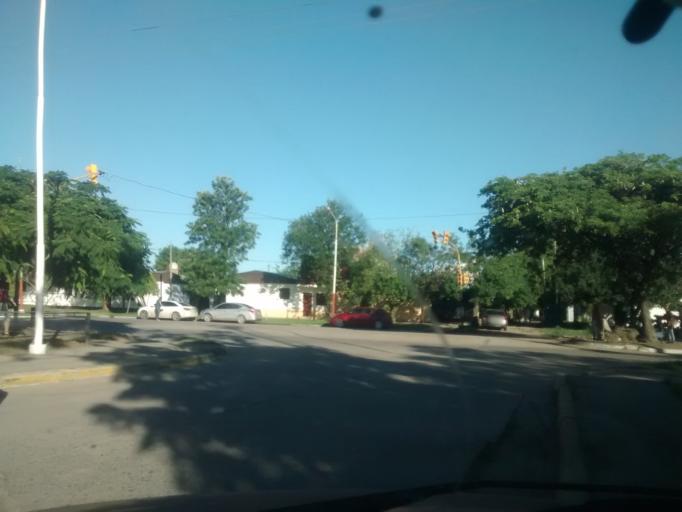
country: AR
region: Chaco
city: Resistencia
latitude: -27.4569
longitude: -59.0220
